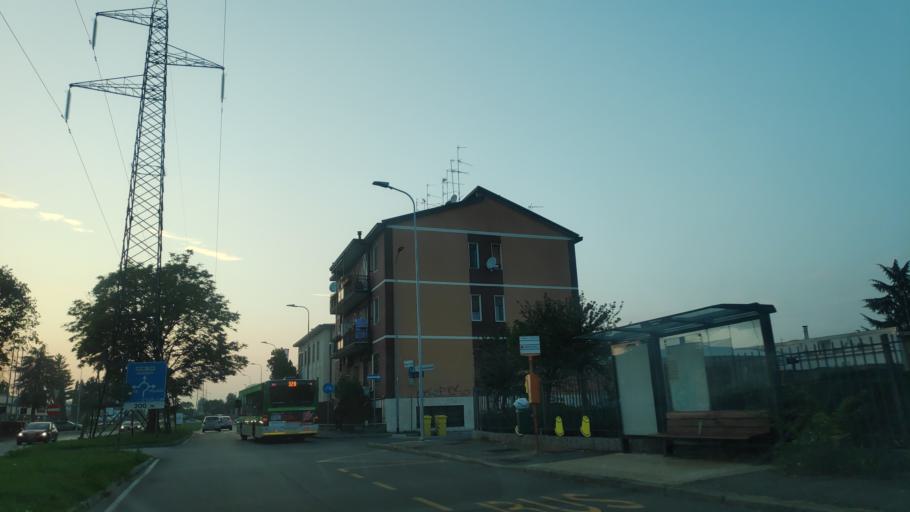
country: IT
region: Lombardy
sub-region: Citta metropolitana di Milano
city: Rozzano
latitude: 45.3946
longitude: 9.1548
